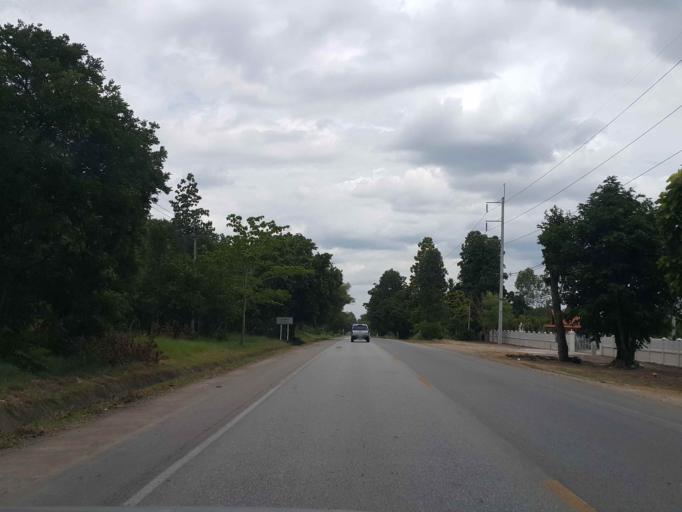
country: TH
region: Chiang Mai
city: Doi Lo
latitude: 18.4190
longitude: 98.8551
